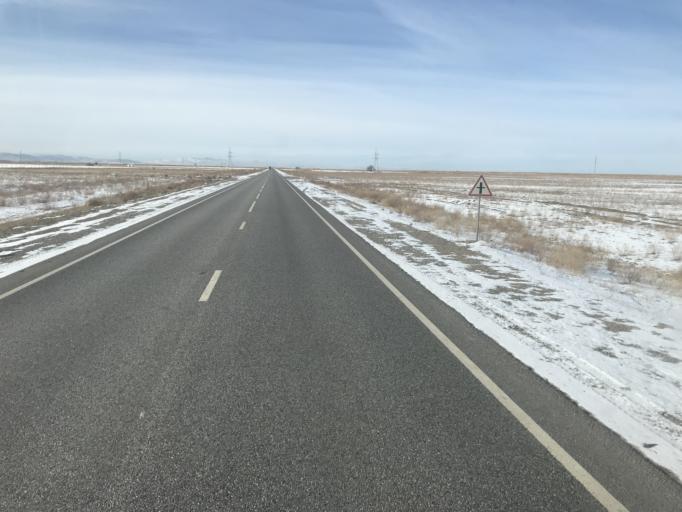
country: KZ
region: Zhambyl
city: Sarykemer
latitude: 43.0456
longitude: 71.4359
